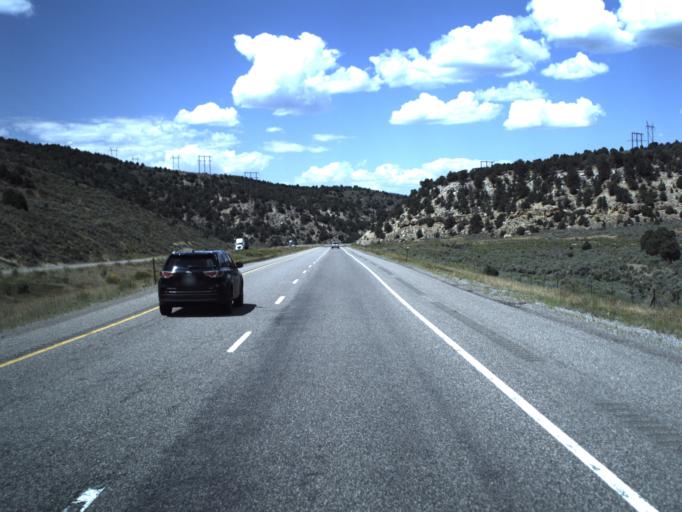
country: US
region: Utah
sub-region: Sevier County
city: Salina
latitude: 38.8063
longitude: -111.5295
